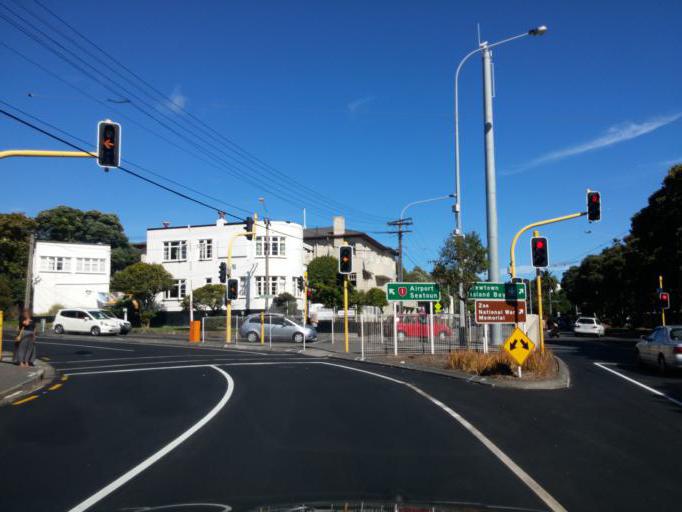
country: NZ
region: Wellington
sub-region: Wellington City
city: Wellington
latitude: -41.3004
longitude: 174.7818
